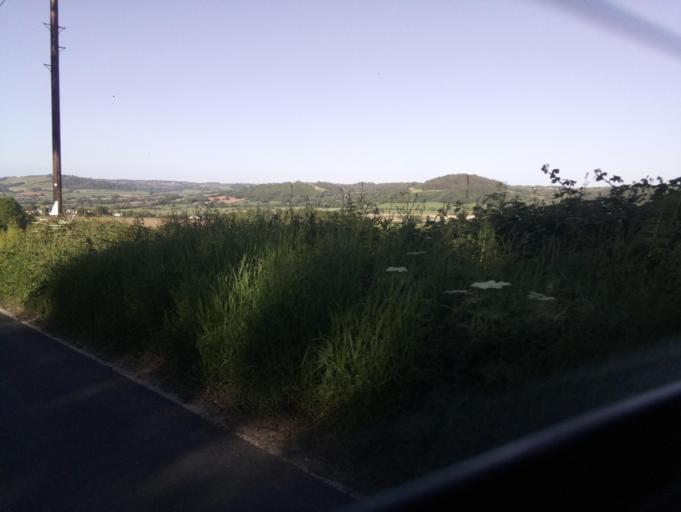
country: GB
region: England
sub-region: Devon
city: Colyton
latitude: 50.7209
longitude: -3.0773
